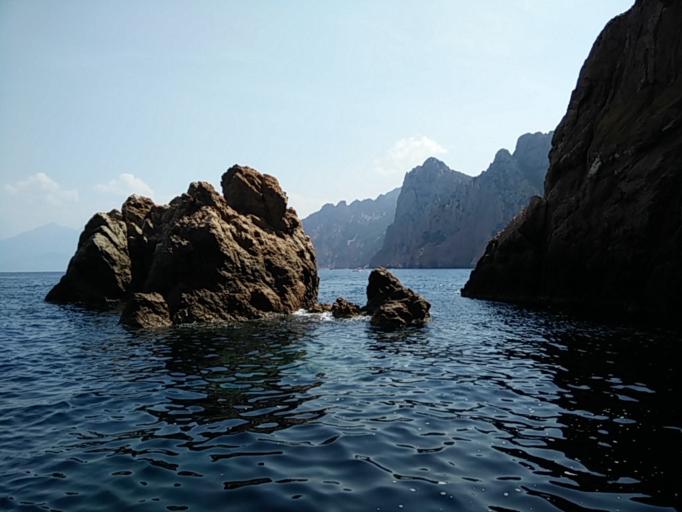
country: FR
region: Corsica
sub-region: Departement de la Corse-du-Sud
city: Cargese
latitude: 42.2385
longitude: 8.5523
